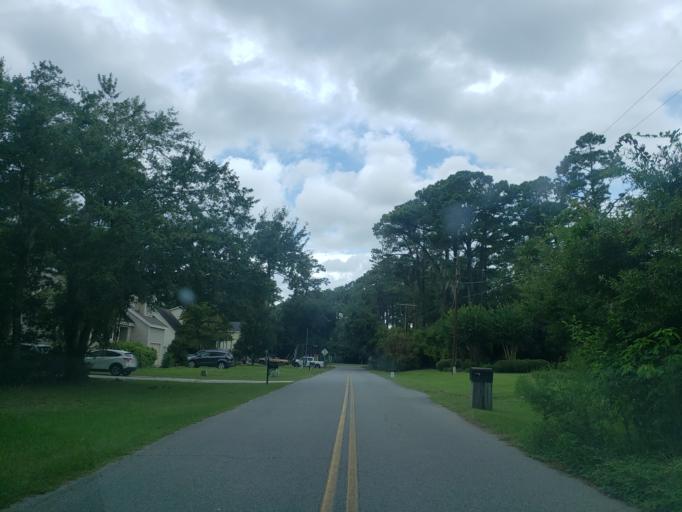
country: US
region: Georgia
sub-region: Chatham County
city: Wilmington Island
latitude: 32.0152
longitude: -80.9592
